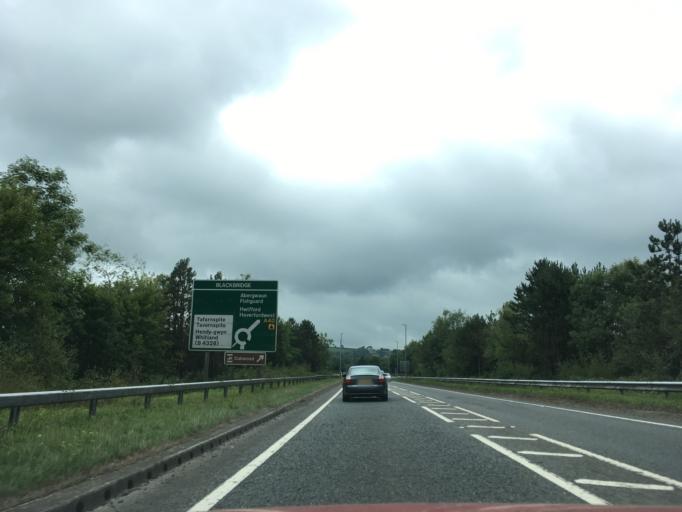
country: GB
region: Wales
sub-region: Carmarthenshire
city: Whitland
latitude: 51.8228
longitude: -4.6238
